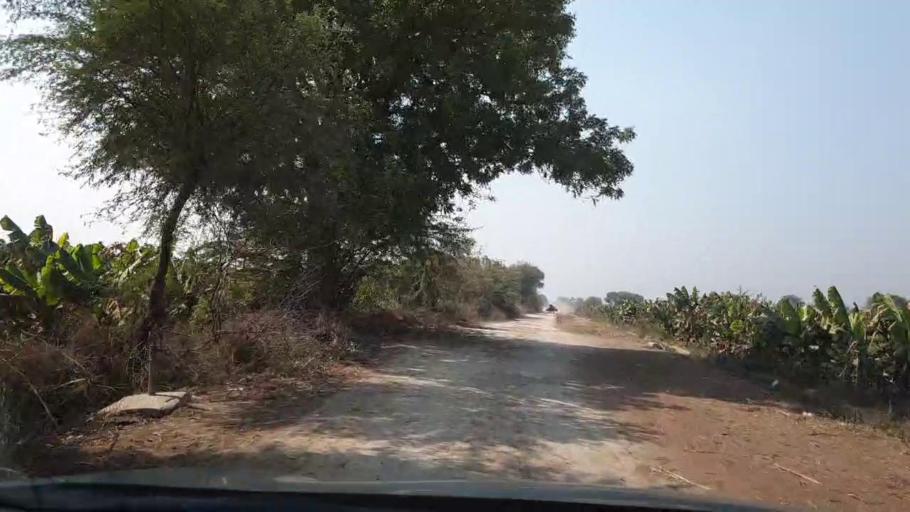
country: PK
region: Sindh
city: Tando Allahyar
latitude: 25.5055
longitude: 68.7898
